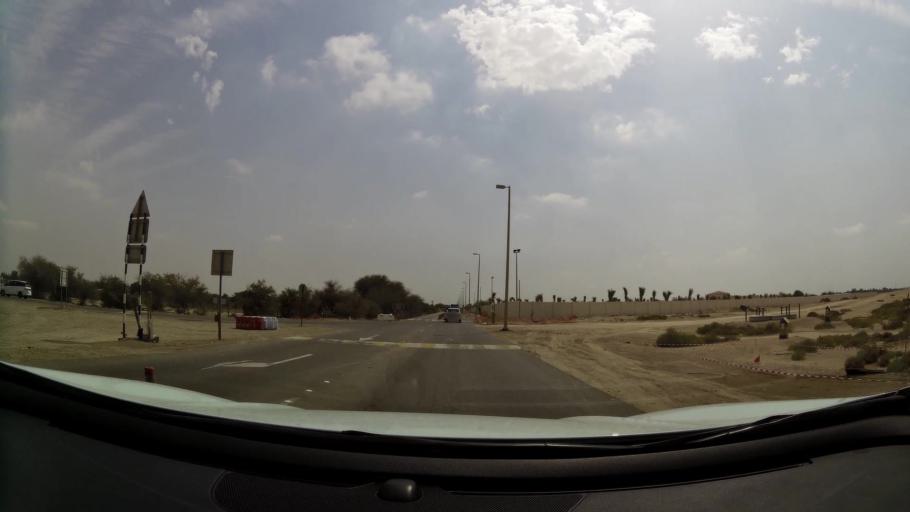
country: AE
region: Abu Dhabi
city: Abu Dhabi
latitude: 24.5224
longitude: 54.6491
